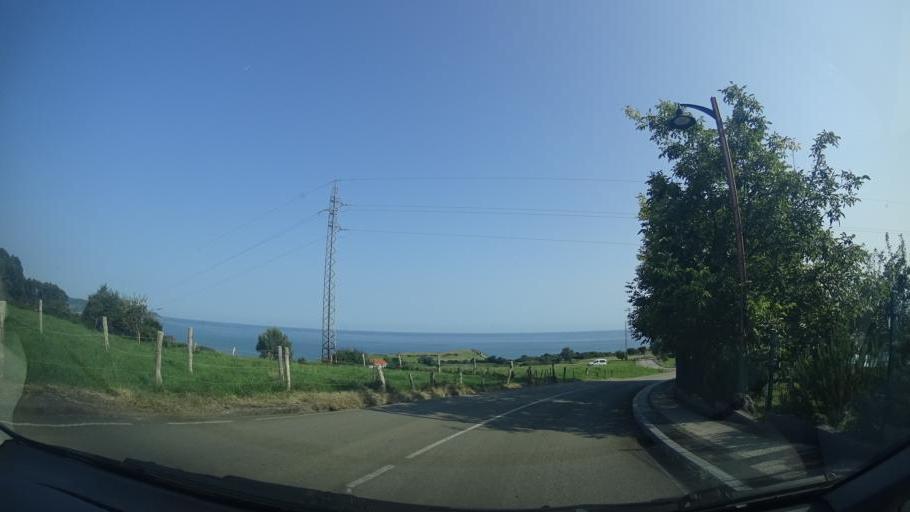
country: ES
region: Asturias
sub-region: Province of Asturias
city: Colunga
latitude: 43.4684
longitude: -5.1897
